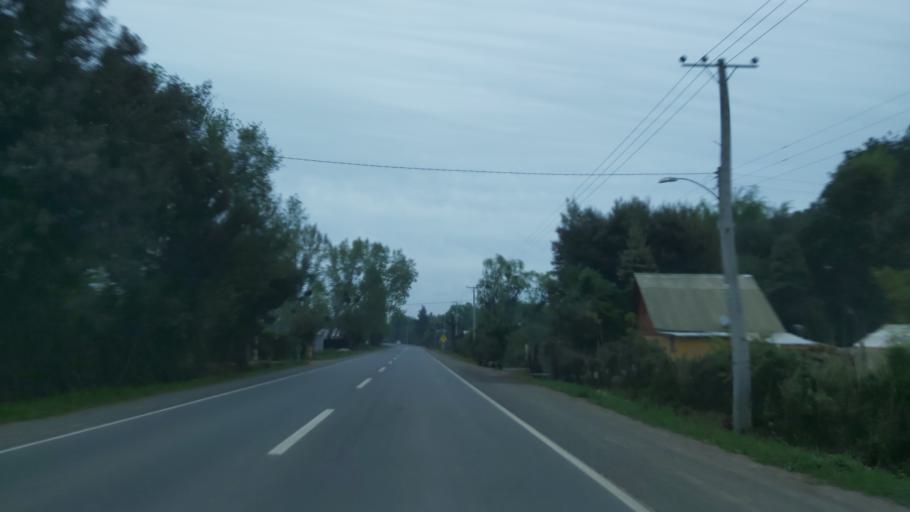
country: CL
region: Maule
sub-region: Provincia de Linares
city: Colbun
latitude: -35.7598
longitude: -71.5060
